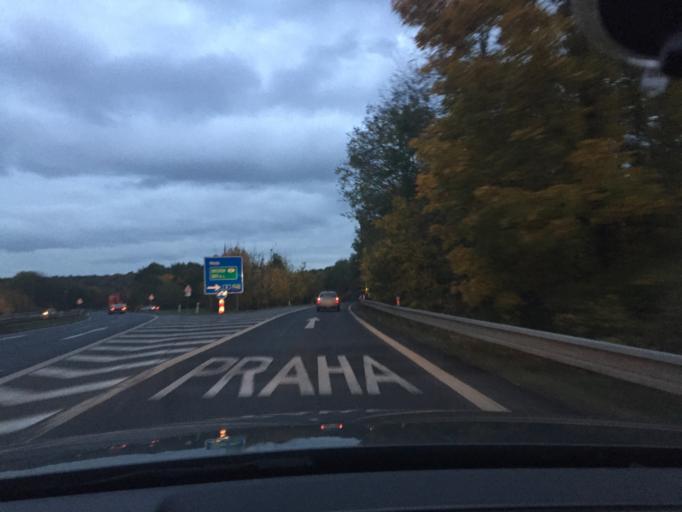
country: CZ
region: Ustecky
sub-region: Okres Teplice
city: Teplice
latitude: 50.6311
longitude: 13.8237
